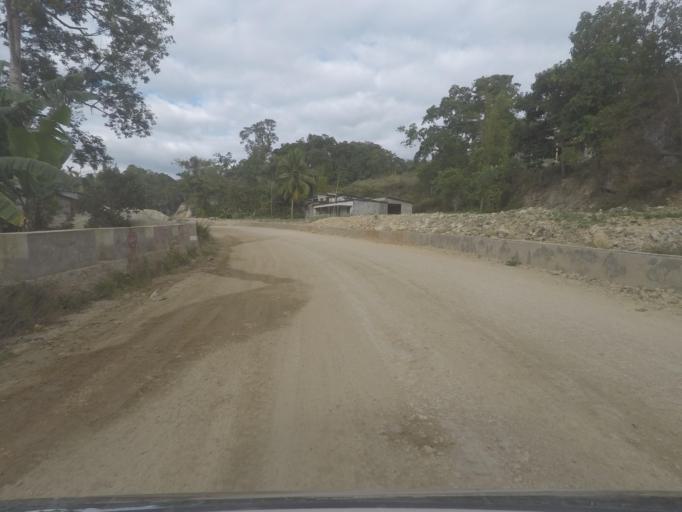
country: TL
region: Baucau
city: Venilale
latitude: -8.6038
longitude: 126.3822
